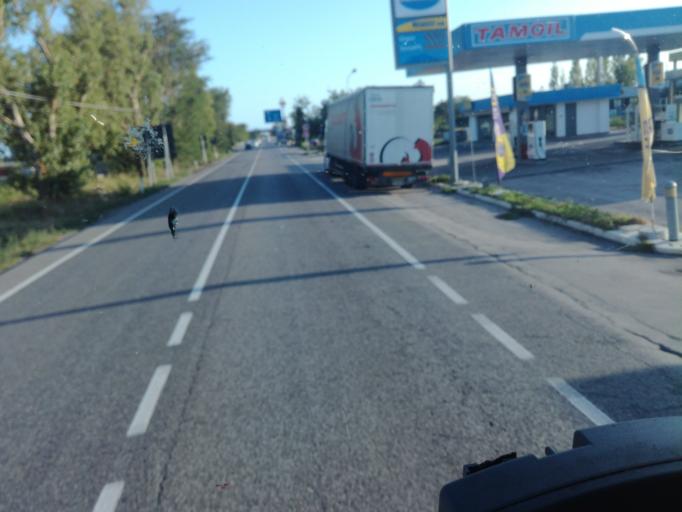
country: IT
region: Emilia-Romagna
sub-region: Provincia di Ferrara
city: Porto Garibaldi
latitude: 44.6927
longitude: 12.2229
